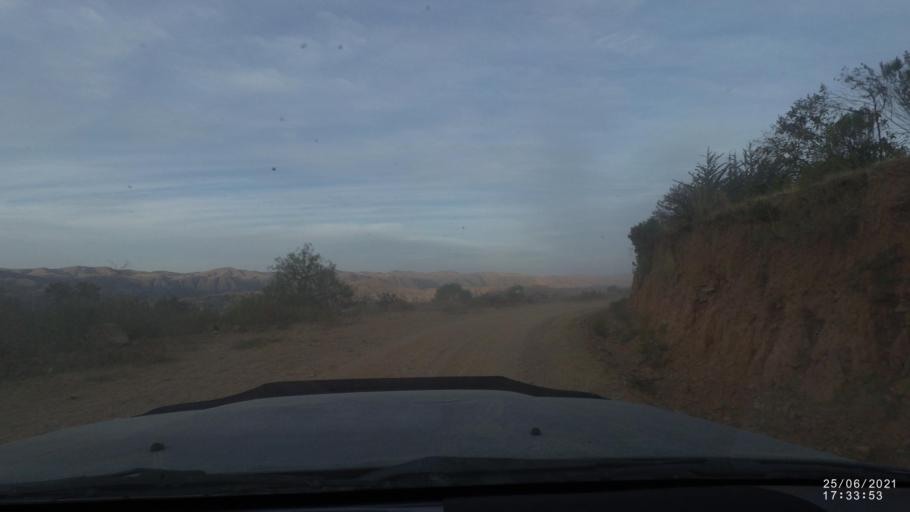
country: BO
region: Cochabamba
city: Mizque
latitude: -17.9447
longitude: -65.6591
